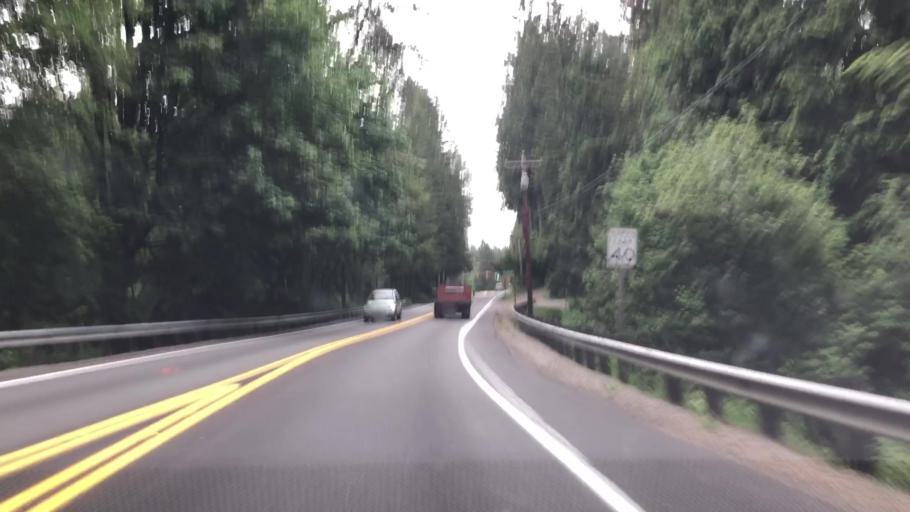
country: US
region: Washington
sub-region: King County
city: Cottage Lake
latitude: 47.7549
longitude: -122.0657
